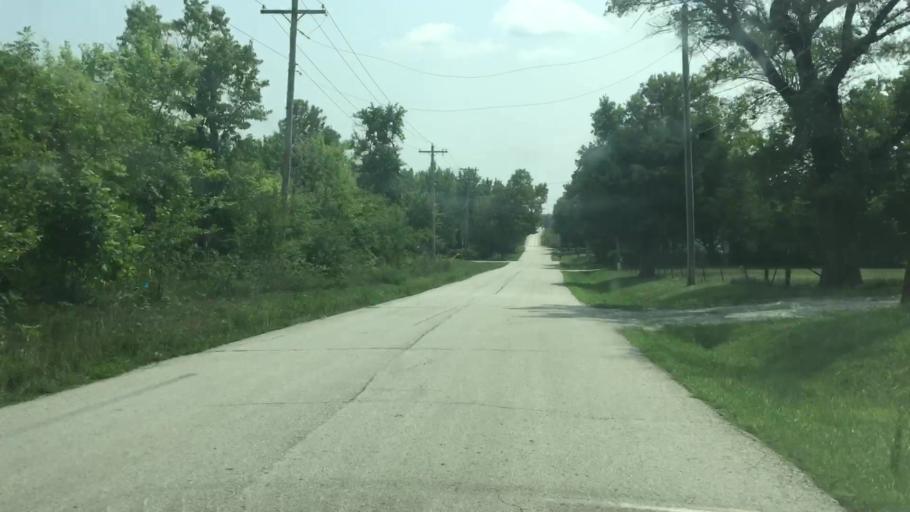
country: US
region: Kansas
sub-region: Douglas County
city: Baldwin City
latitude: 38.7742
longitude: -95.2049
